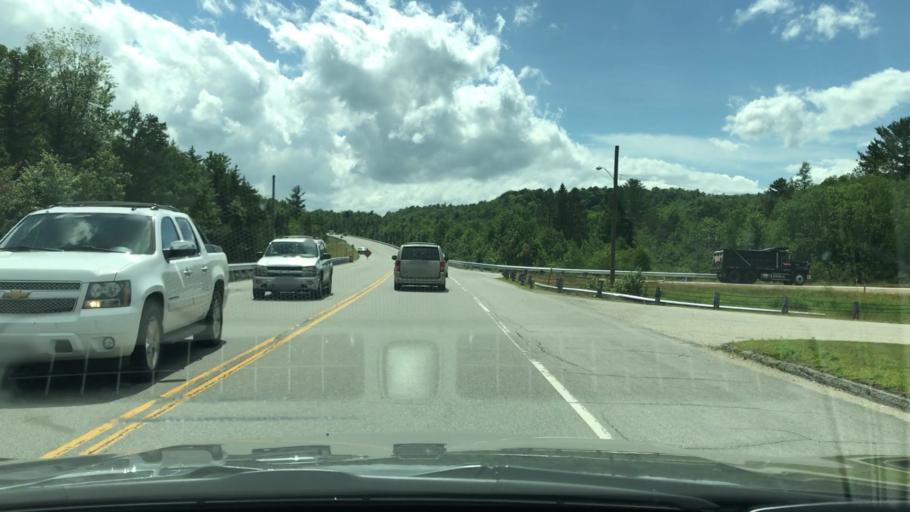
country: US
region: New Hampshire
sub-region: Coos County
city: Jefferson
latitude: 44.3645
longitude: -71.3289
